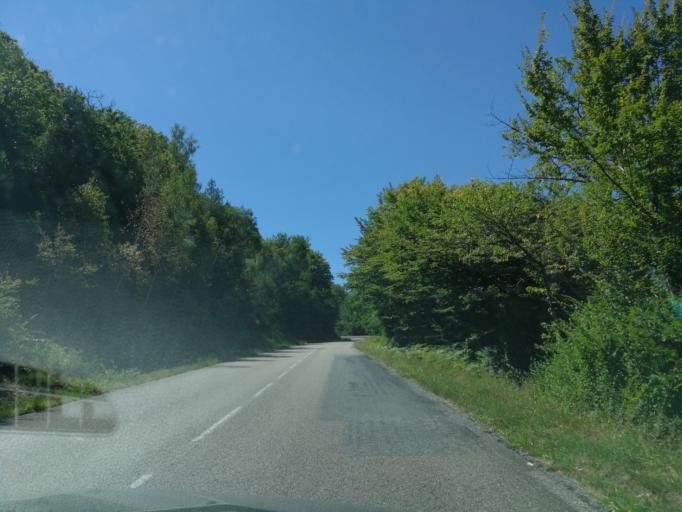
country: FR
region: Limousin
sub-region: Departement de la Correze
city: Argentat
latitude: 45.0639
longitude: 1.9473
